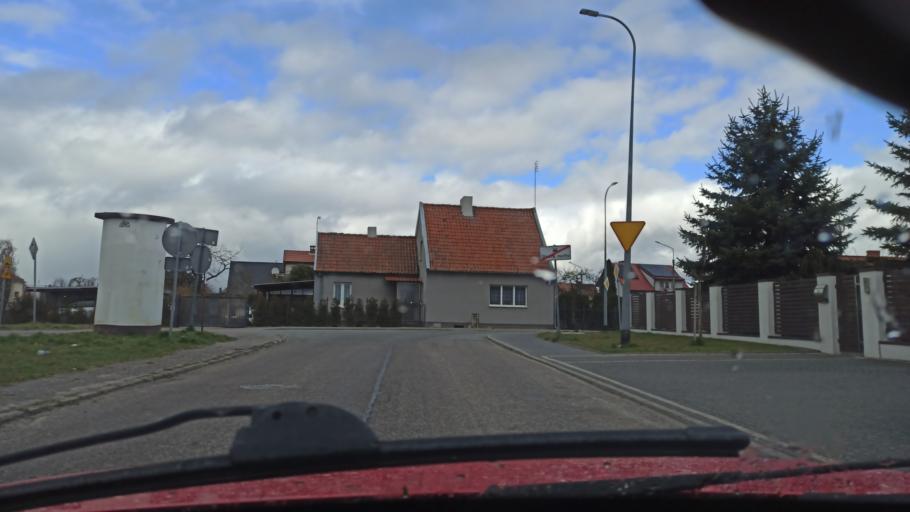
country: PL
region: Warmian-Masurian Voivodeship
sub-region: Powiat elblaski
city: Elblag
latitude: 54.1474
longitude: 19.4077
